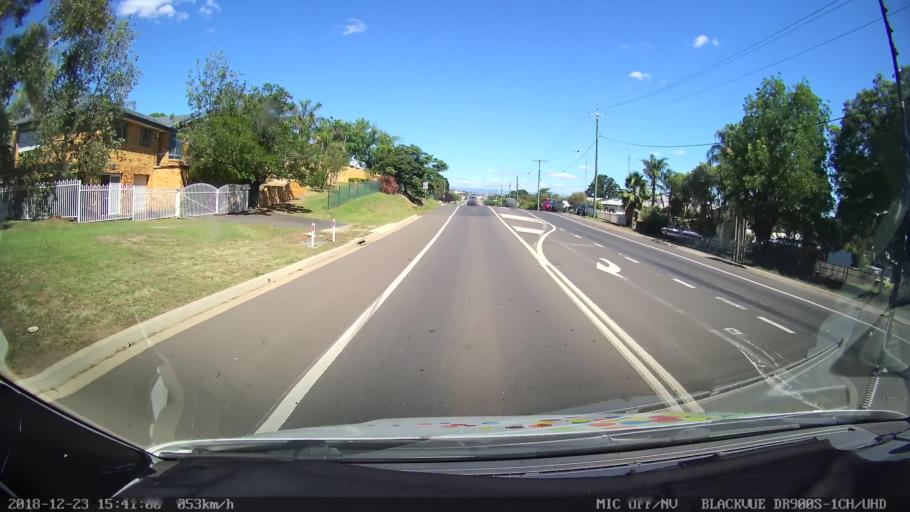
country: AU
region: New South Wales
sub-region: Tamworth Municipality
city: Tamworth
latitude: -31.0741
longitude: 150.9137
